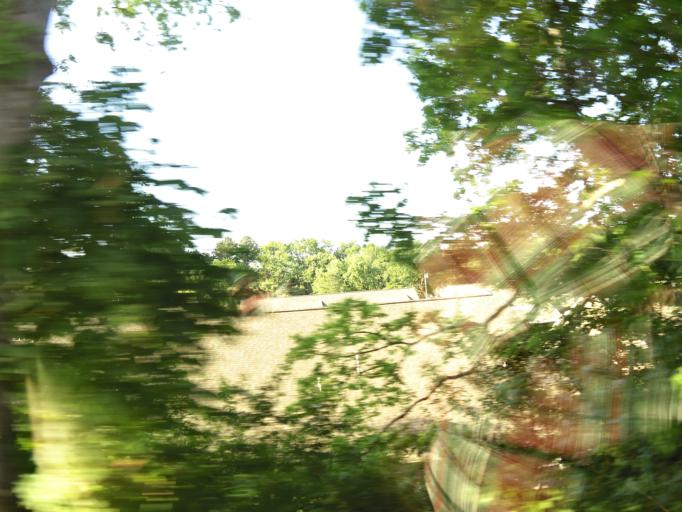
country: US
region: Tennessee
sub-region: Sevier County
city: Pigeon Forge
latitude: 35.8160
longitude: -83.5831
